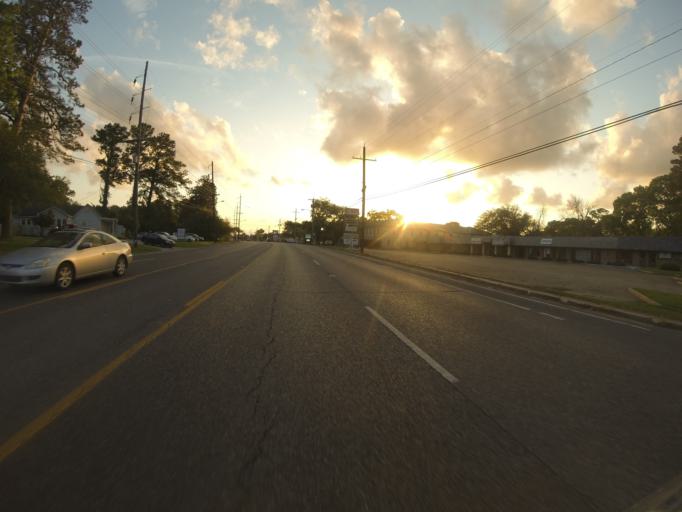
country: US
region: Louisiana
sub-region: Lafayette Parish
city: Lafayette
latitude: 30.2090
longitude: -92.0349
